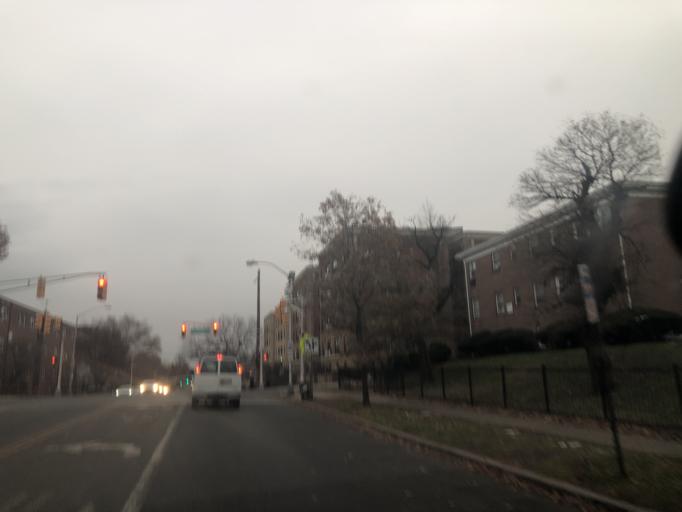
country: US
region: New Jersey
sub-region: Essex County
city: East Orange
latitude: 40.7676
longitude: -74.2069
